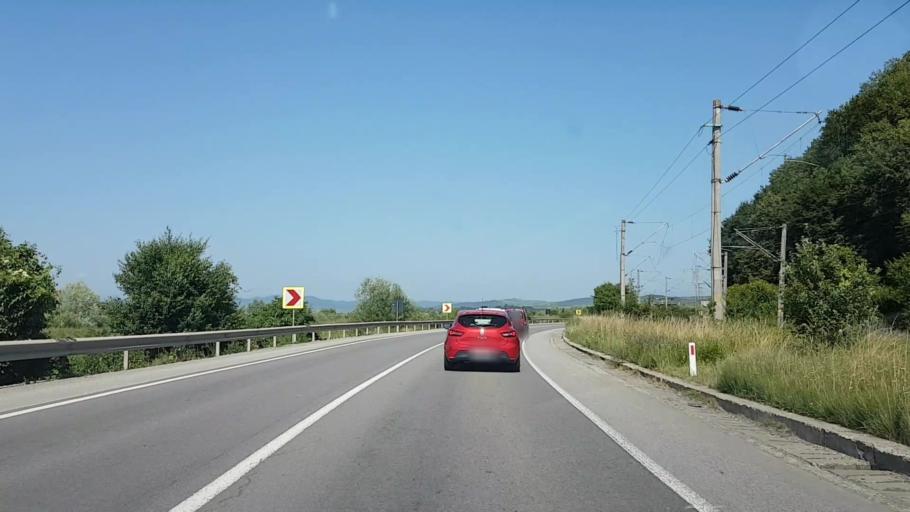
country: RO
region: Bistrita-Nasaud
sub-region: Comuna Beclean
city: Beclean
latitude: 47.1862
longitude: 24.1954
